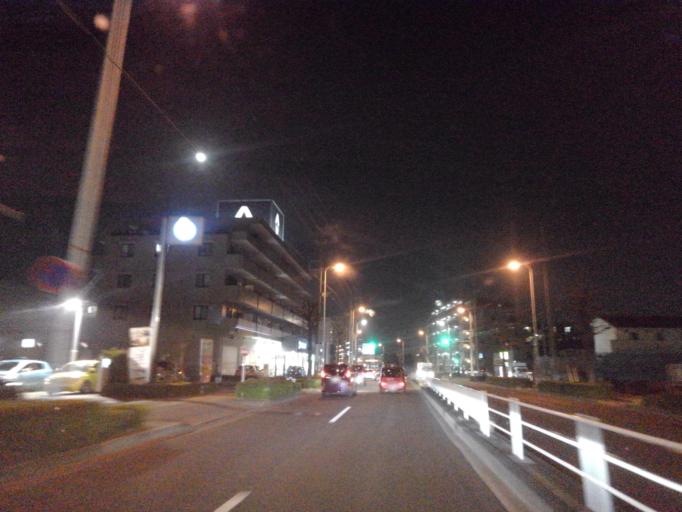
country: JP
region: Tokyo
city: Chofugaoka
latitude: 35.6380
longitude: 139.5059
